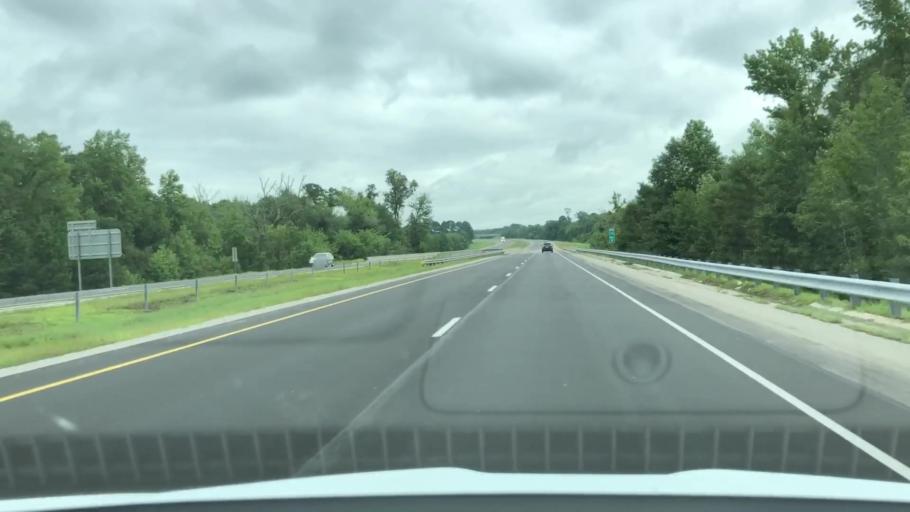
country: US
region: North Carolina
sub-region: Wilson County
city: Lucama
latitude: 35.6365
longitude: -77.9692
